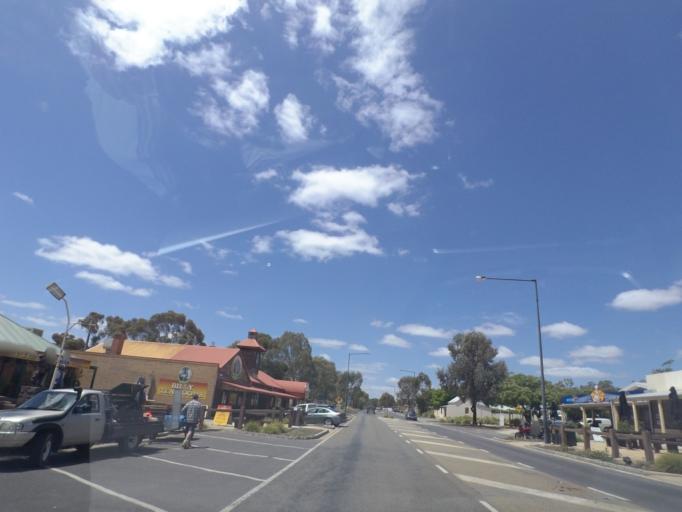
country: AU
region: Victoria
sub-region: Wangaratta
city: Wangaratta
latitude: -36.4640
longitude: 146.2218
